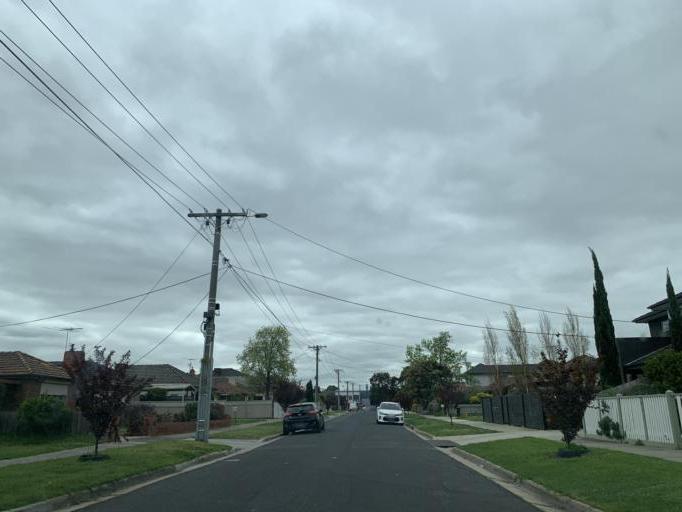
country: AU
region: Victoria
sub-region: Moreland
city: Pascoe Vale South
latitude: -37.7316
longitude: 144.9484
